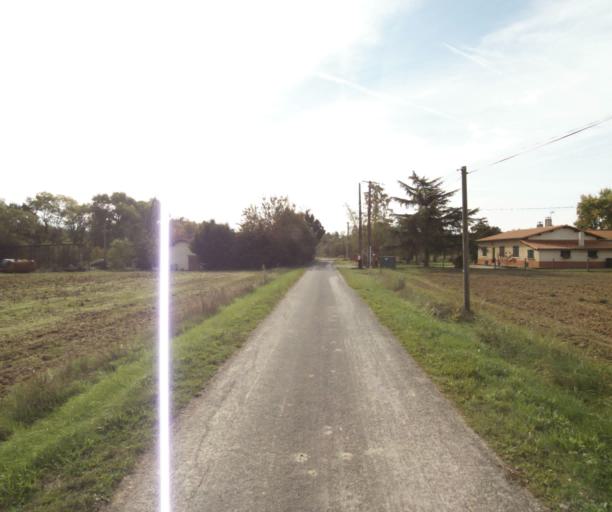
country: FR
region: Midi-Pyrenees
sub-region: Departement du Tarn-et-Garonne
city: Orgueil
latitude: 43.8925
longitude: 1.4132
